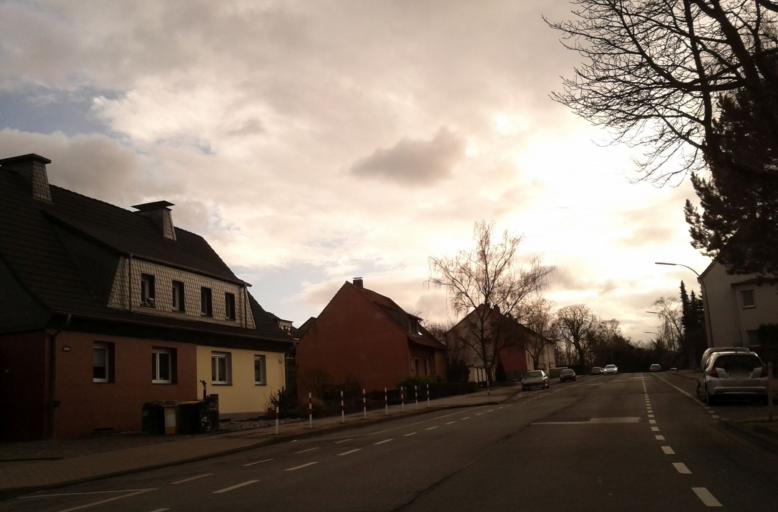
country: DE
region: North Rhine-Westphalia
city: Lanstrop
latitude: 51.5539
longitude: 7.5129
